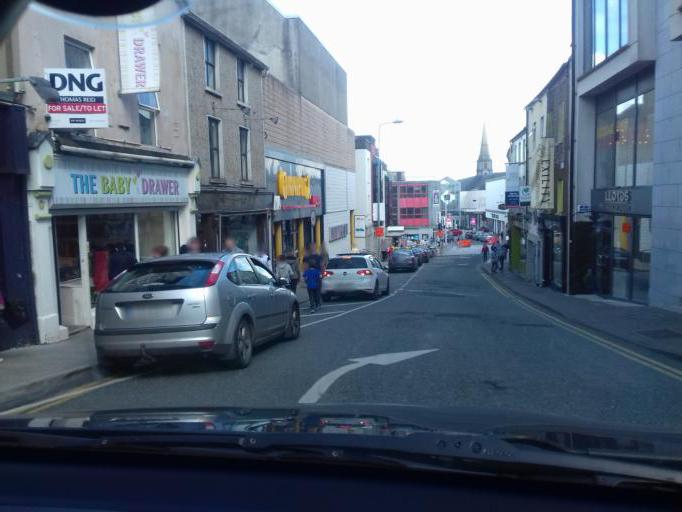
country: IE
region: Munster
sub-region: Waterford
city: Waterford
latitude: 52.2601
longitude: -7.1130
